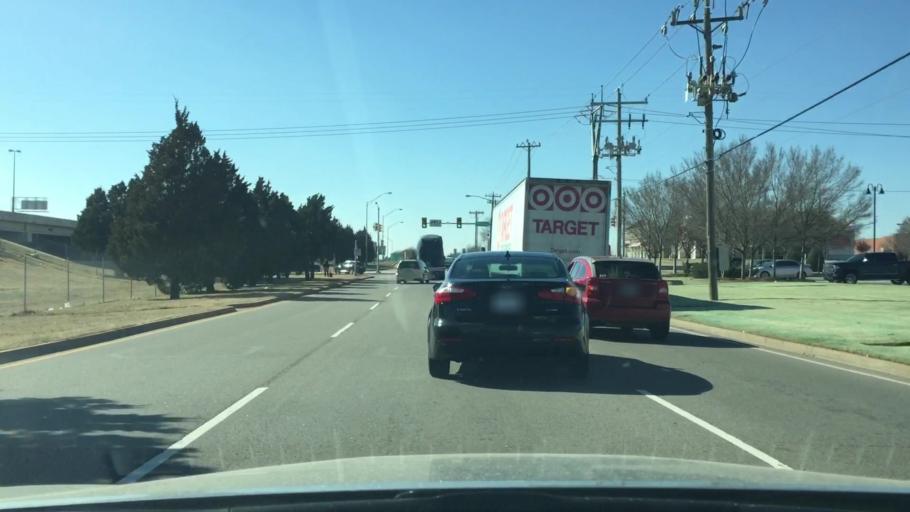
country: US
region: Oklahoma
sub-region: Oklahoma County
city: The Village
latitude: 35.6097
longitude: -97.5482
